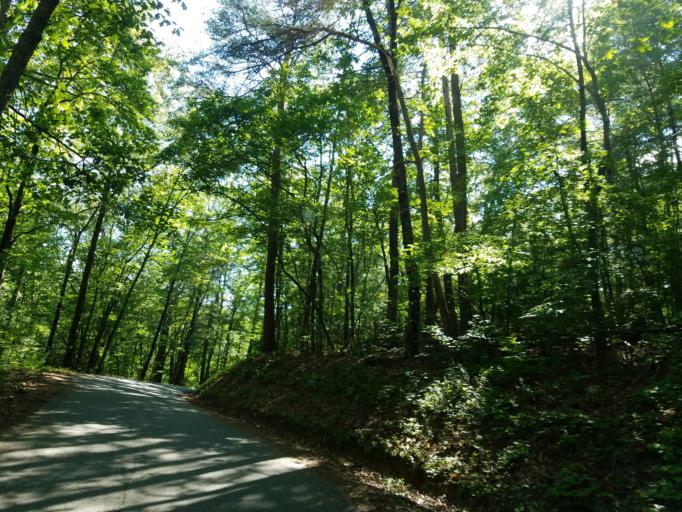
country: US
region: Georgia
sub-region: Dawson County
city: Dawsonville
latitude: 34.5705
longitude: -84.1593
